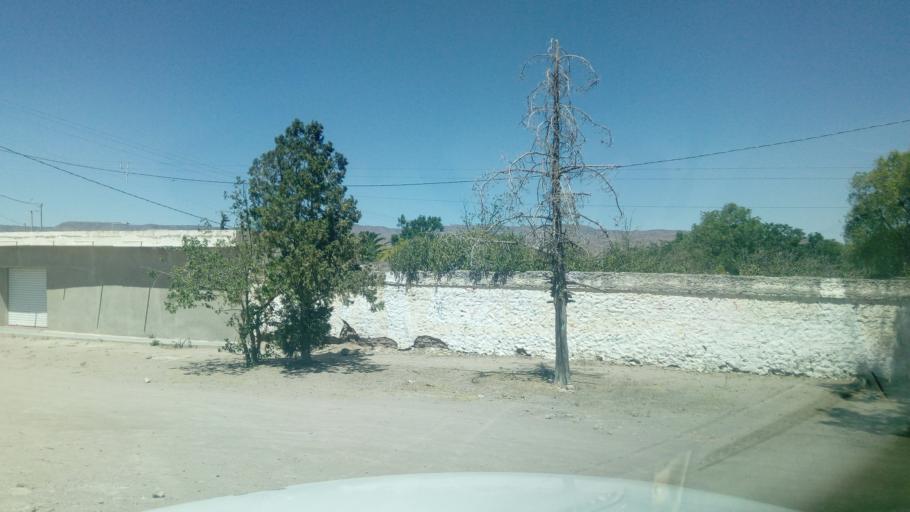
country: MX
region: Durango
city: Victoria de Durango
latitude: 24.1706
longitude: -104.7016
